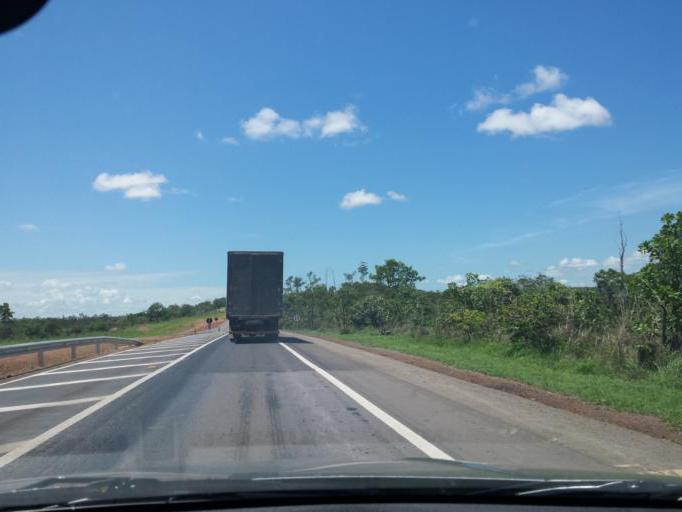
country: BR
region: Goias
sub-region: Luziania
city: Luziania
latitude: -16.5115
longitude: -47.8095
